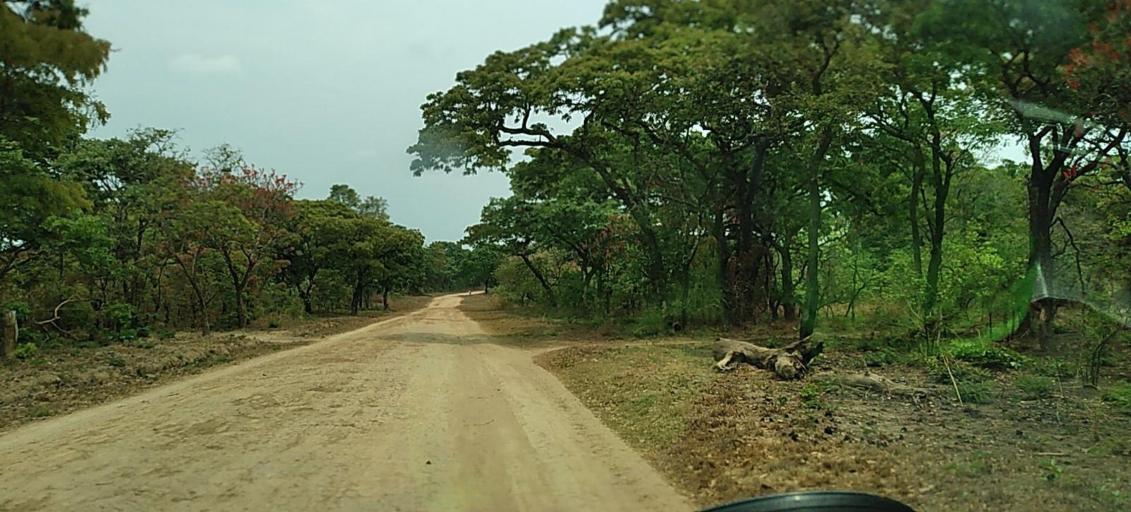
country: ZM
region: North-Western
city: Solwezi
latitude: -12.8237
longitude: 26.5373
